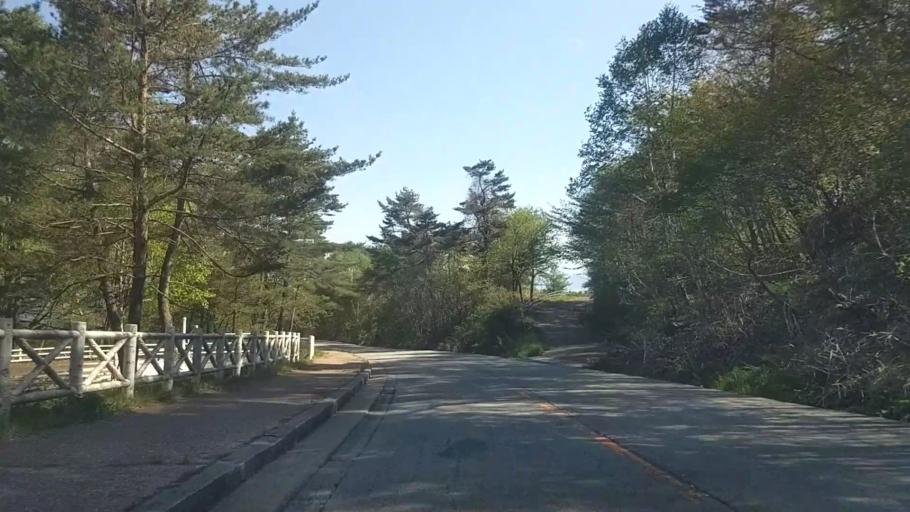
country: JP
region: Yamanashi
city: Nirasaki
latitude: 35.9273
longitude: 138.4071
